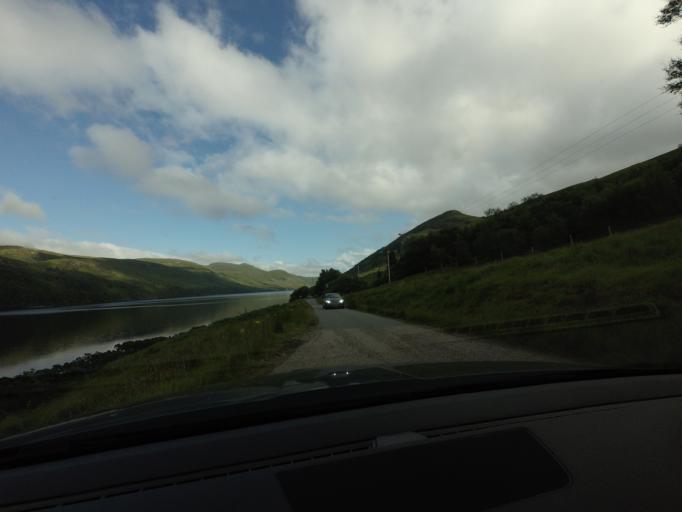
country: GB
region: Scotland
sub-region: Highland
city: Ullapool
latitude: 58.2958
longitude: -4.8742
